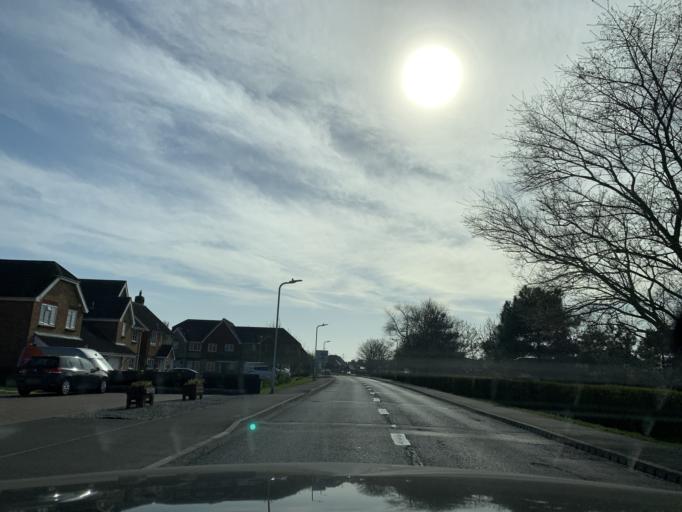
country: GB
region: England
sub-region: Kent
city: Lydd
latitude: 50.9534
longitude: 0.9142
